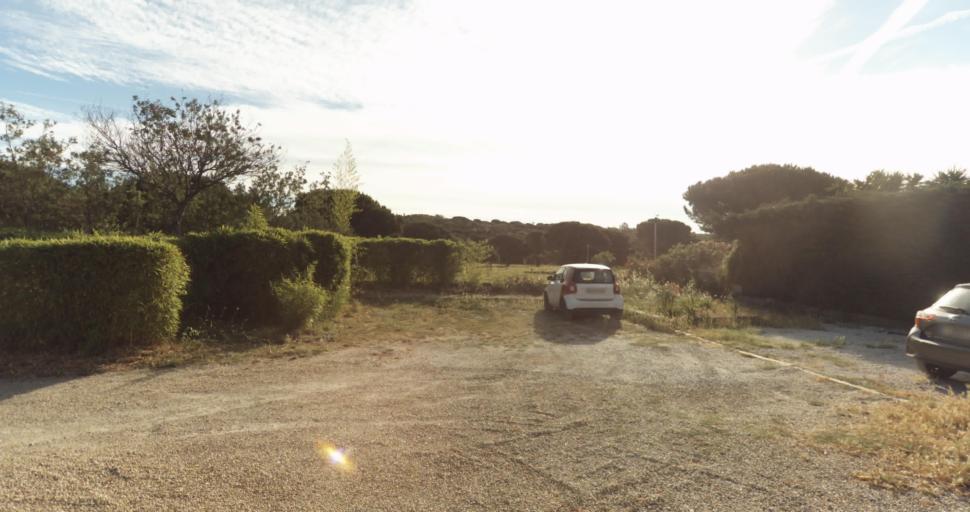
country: FR
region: Provence-Alpes-Cote d'Azur
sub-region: Departement du Var
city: Saint-Tropez
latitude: 43.2545
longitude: 6.6337
